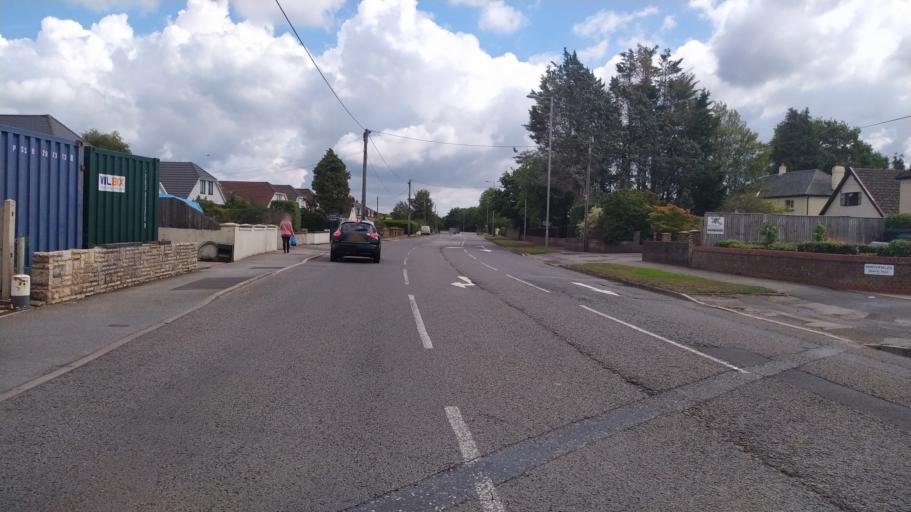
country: GB
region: England
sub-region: Dorset
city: Wimborne Minster
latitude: 50.7989
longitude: -1.9505
